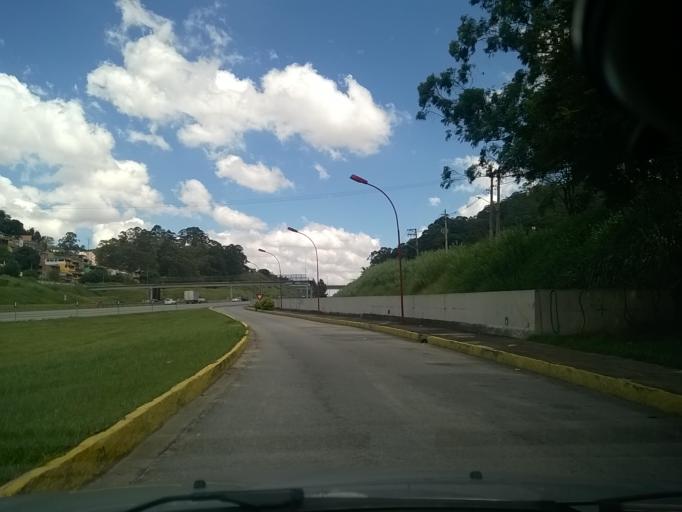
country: BR
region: Sao Paulo
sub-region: Caieiras
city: Caieiras
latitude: -23.4464
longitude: -46.7561
